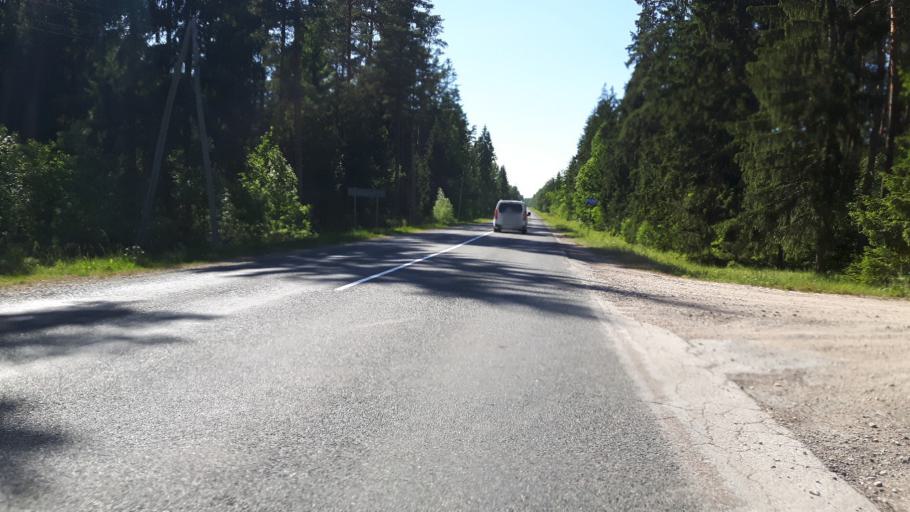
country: LV
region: Talsu Rajons
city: Stende
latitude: 57.0865
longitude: 22.4164
